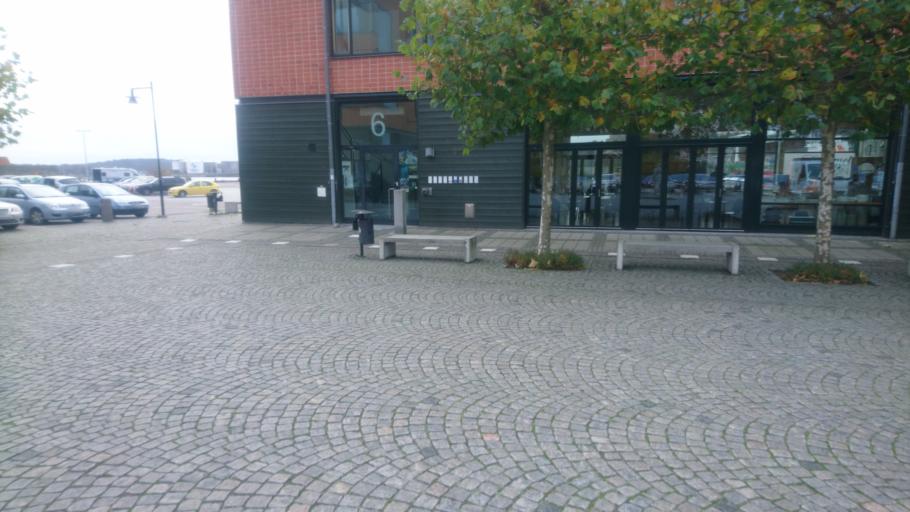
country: SE
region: Blekinge
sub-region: Karlshamns Kommun
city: Karlshamn
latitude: 56.1642
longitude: 14.8664
